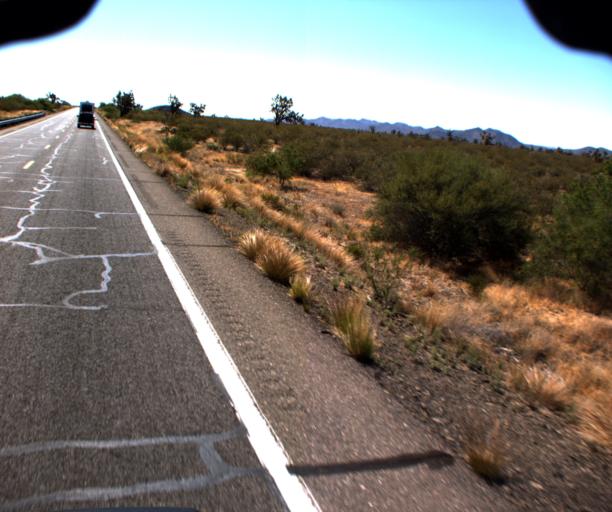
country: US
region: Arizona
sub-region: Yavapai County
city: Congress
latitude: 34.1829
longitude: -113.0404
